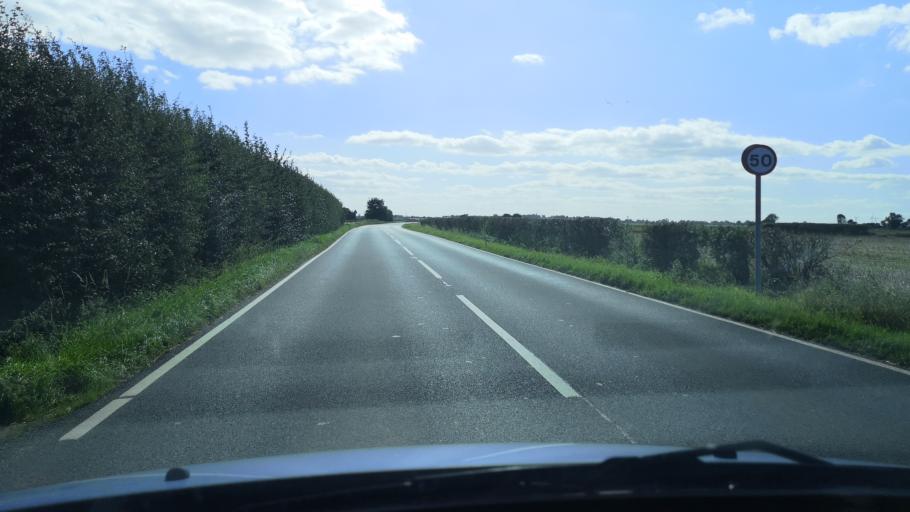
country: GB
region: England
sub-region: North Lincolnshire
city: Eastoft
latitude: 53.6281
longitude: -0.7996
